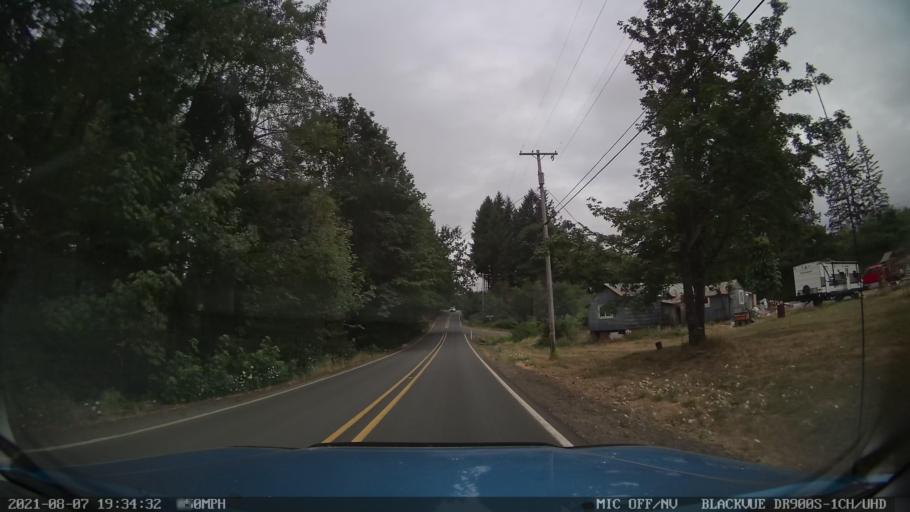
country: US
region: Oregon
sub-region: Linn County
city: Lyons
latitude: 44.9186
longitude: -122.6559
